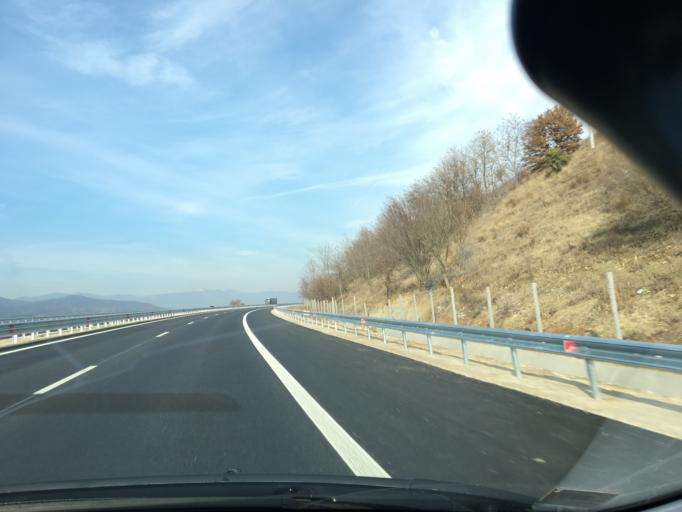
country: BG
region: Blagoevgrad
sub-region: Obshtina Sandanski
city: Sandanski
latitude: 41.5590
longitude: 23.2427
